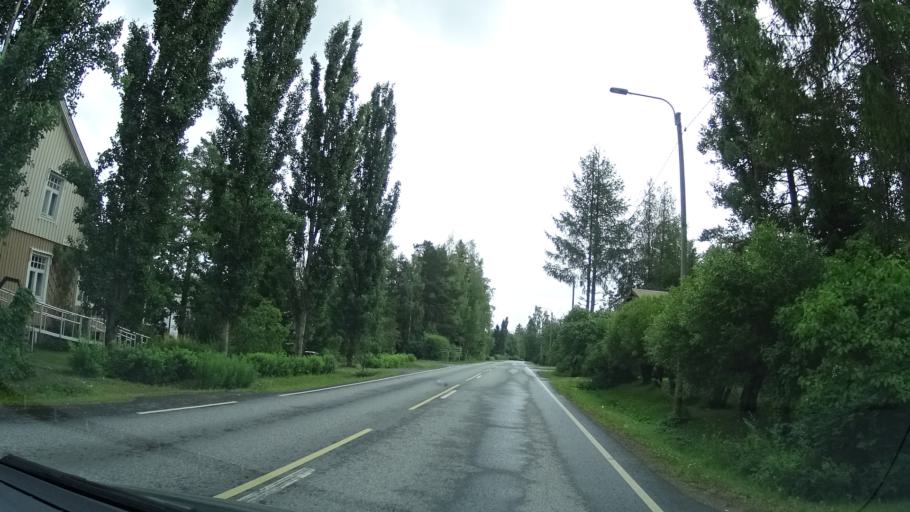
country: FI
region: Pirkanmaa
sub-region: Lounais-Pirkanmaa
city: Punkalaidun
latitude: 61.1022
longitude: 23.2834
